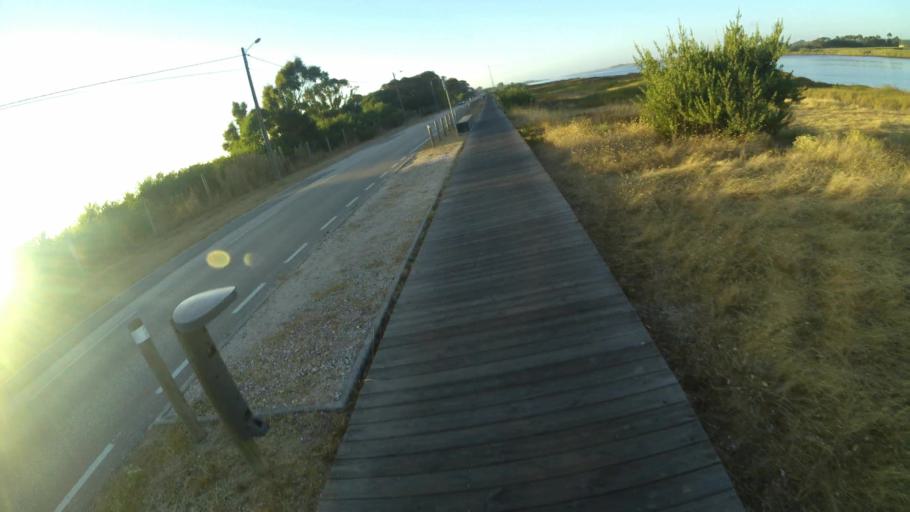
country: PT
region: Aveiro
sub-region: Ilhavo
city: Gafanha da Encarnacao
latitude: 40.5658
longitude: -8.7569
